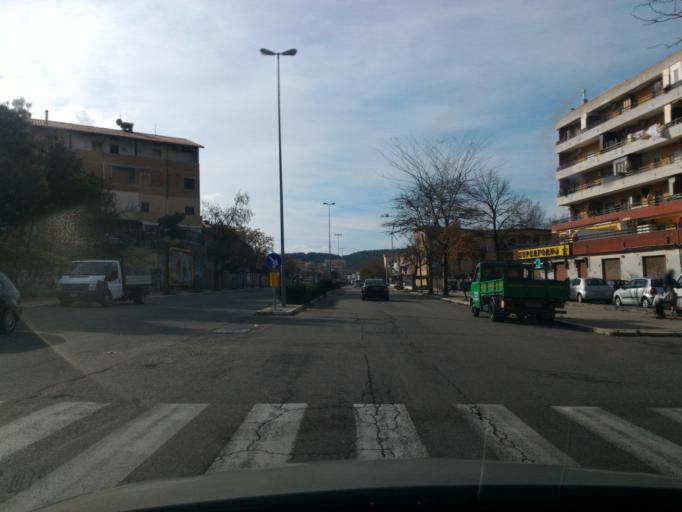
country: IT
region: Calabria
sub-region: Provincia di Crotone
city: Crotone
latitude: 39.0795
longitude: 17.1094
